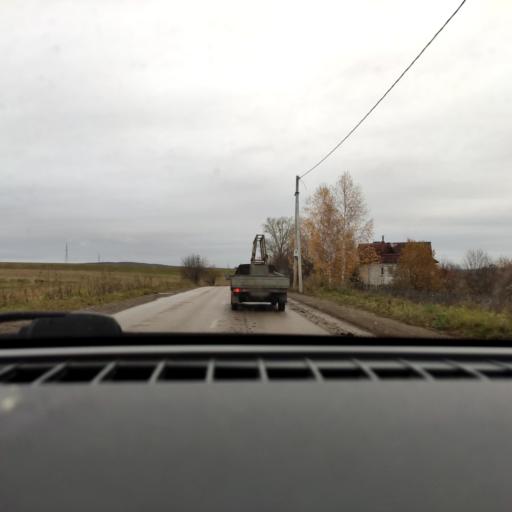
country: RU
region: Perm
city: Ferma
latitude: 57.9205
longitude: 56.3274
